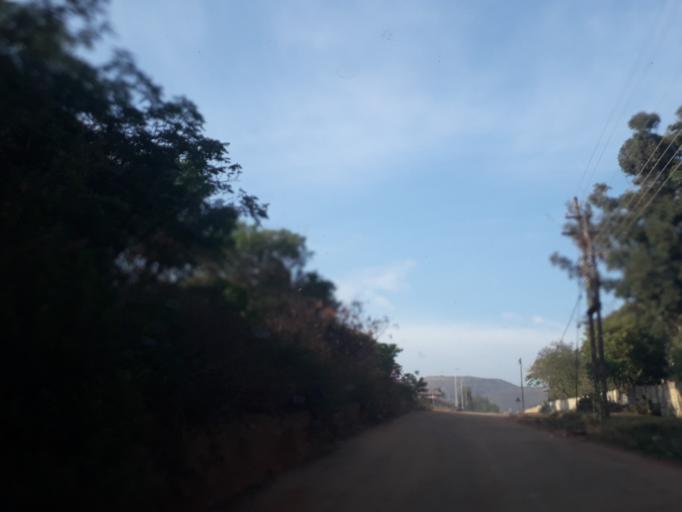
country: ZA
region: Gauteng
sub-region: City of Johannesburg Metropolitan Municipality
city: Roodepoort
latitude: -26.0998
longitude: 27.8945
